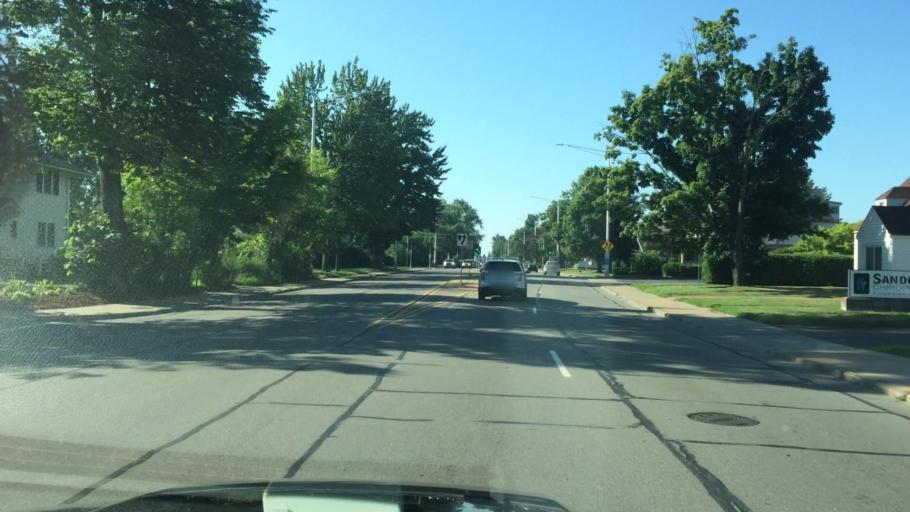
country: US
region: Wisconsin
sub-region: Marathon County
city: Wausau
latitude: 44.9463
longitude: -89.6209
